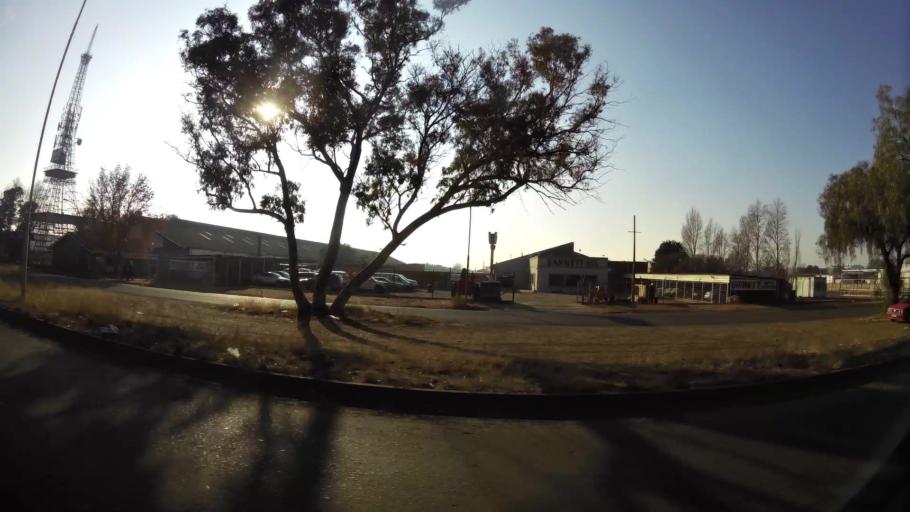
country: ZA
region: Orange Free State
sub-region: Mangaung Metropolitan Municipality
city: Bloemfontein
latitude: -29.1477
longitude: 26.2168
